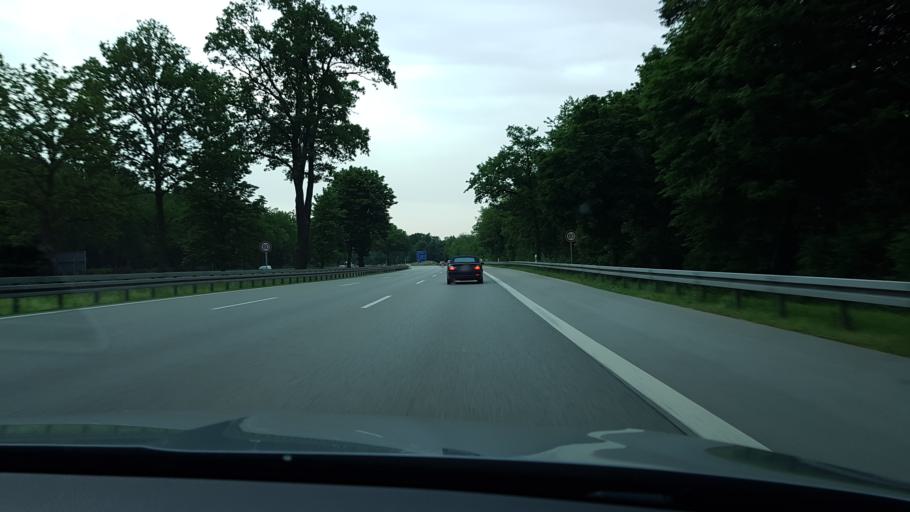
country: DE
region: Bavaria
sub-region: Upper Bavaria
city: Neuried
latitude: 48.0736
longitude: 11.4847
